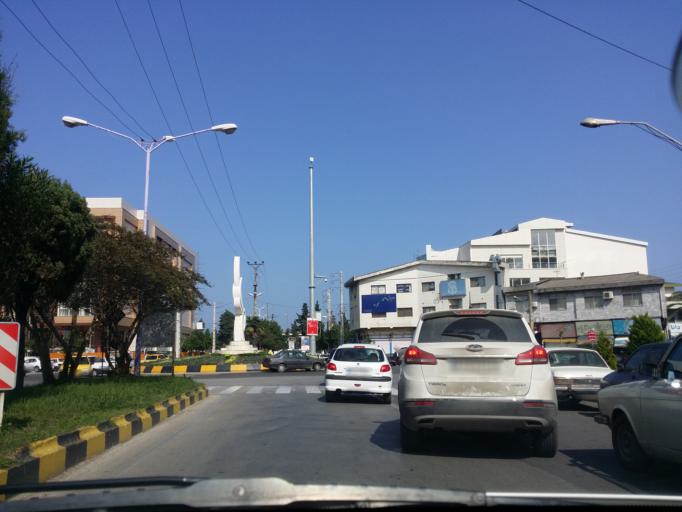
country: IR
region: Mazandaran
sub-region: Nowshahr
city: Nowshahr
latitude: 36.6525
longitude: 51.4951
